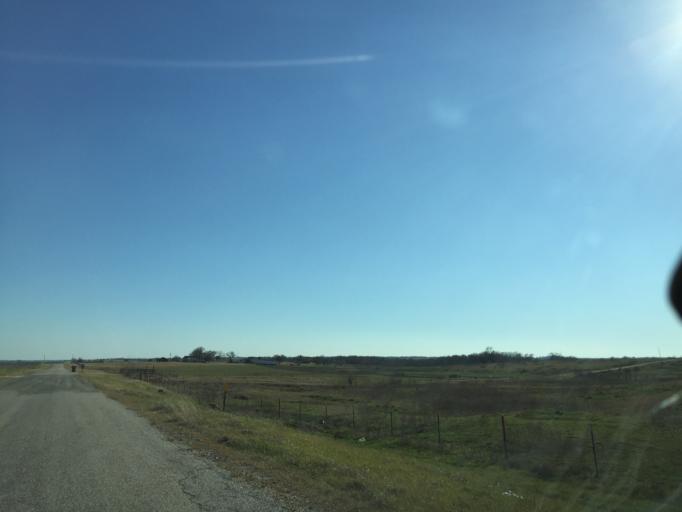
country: US
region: Texas
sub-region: Milam County
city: Thorndale
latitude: 30.5540
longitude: -97.2988
